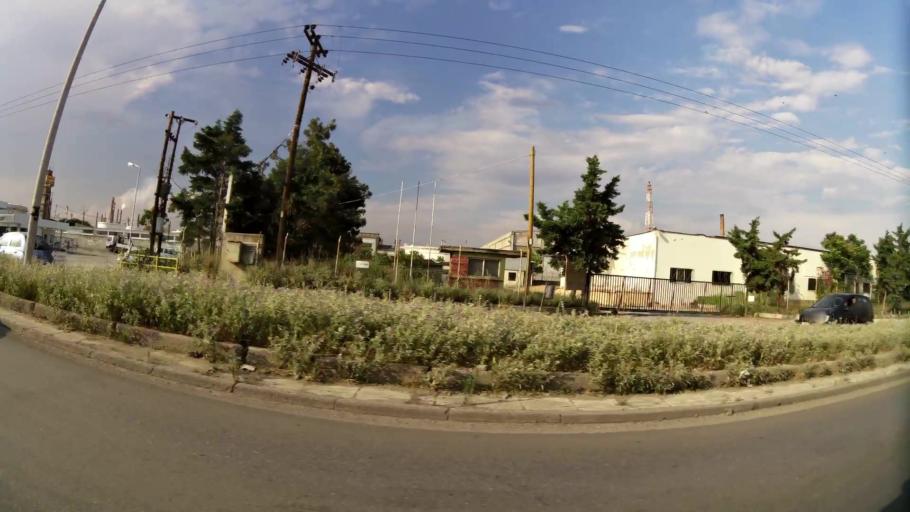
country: GR
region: Central Macedonia
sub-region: Nomos Thessalonikis
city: Menemeni
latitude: 40.6734
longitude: 22.8801
